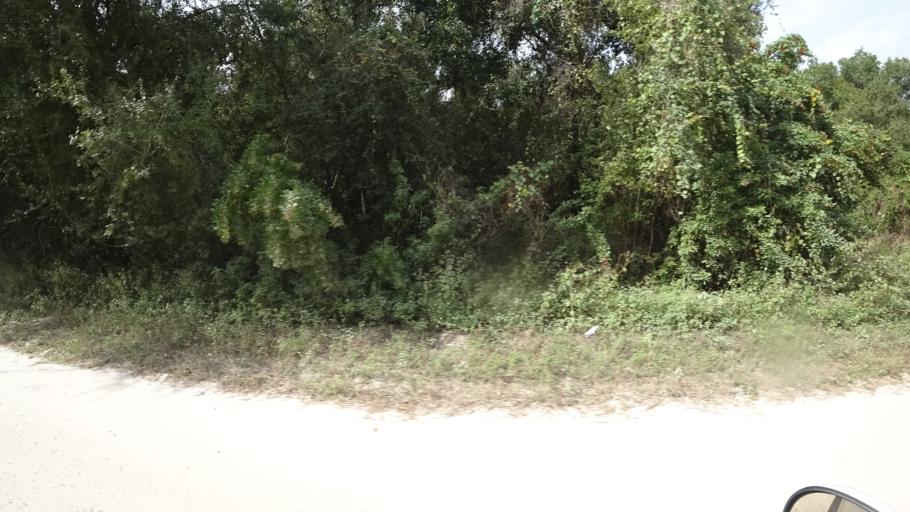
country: US
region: Florida
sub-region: Hillsborough County
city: Wimauma
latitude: 27.5989
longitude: -82.3119
